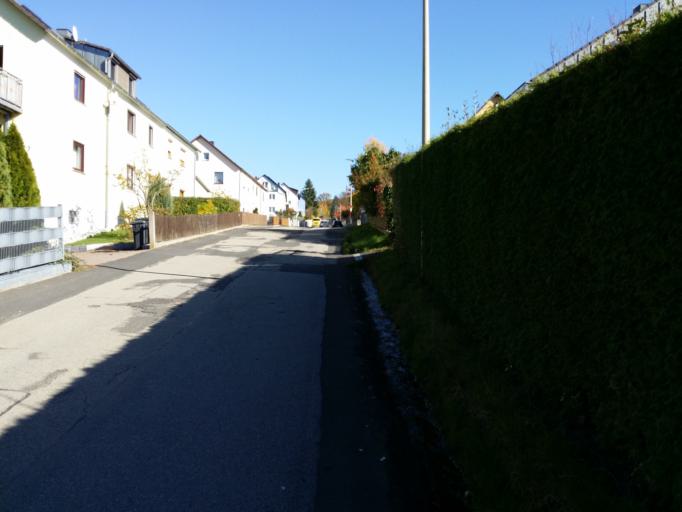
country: DE
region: Bavaria
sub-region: Upper Palatinate
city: Amberg
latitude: 49.4592
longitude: 11.8533
